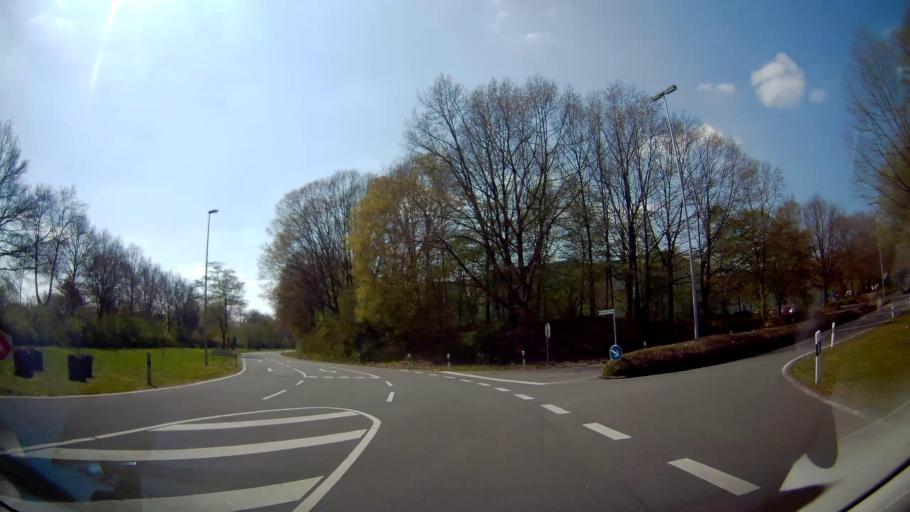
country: DE
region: North Rhine-Westphalia
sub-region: Regierungsbezirk Munster
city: Klein Reken
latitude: 51.7293
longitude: 7.0479
